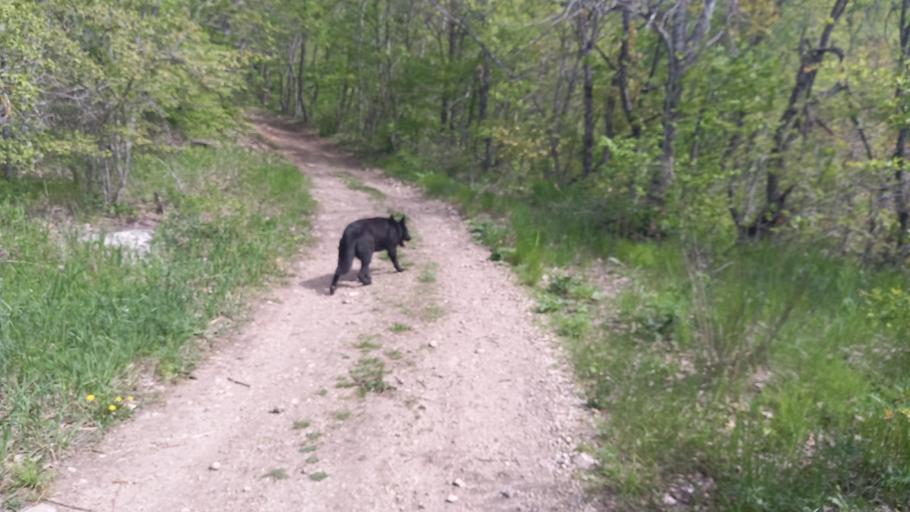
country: RU
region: Stavropol'skiy
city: Zheleznovodsk
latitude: 44.0899
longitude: 43.0298
